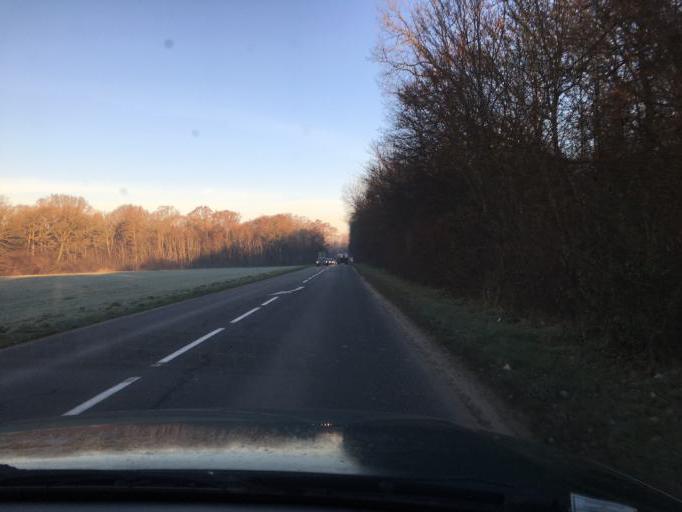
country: FR
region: Centre
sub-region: Departement du Loiret
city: Saran
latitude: 47.9648
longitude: 1.8694
